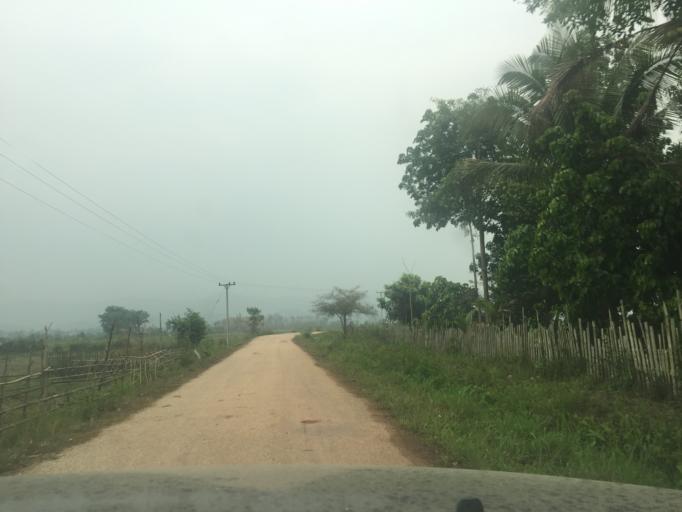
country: LA
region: Xiagnabouli
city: Sainyabuli
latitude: 19.0433
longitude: 101.5141
